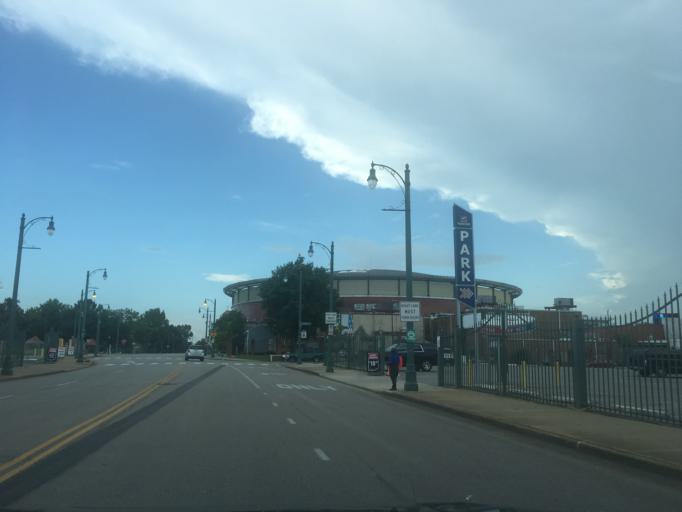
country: US
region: Tennessee
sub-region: Shelby County
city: Memphis
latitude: 35.1407
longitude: -90.0494
